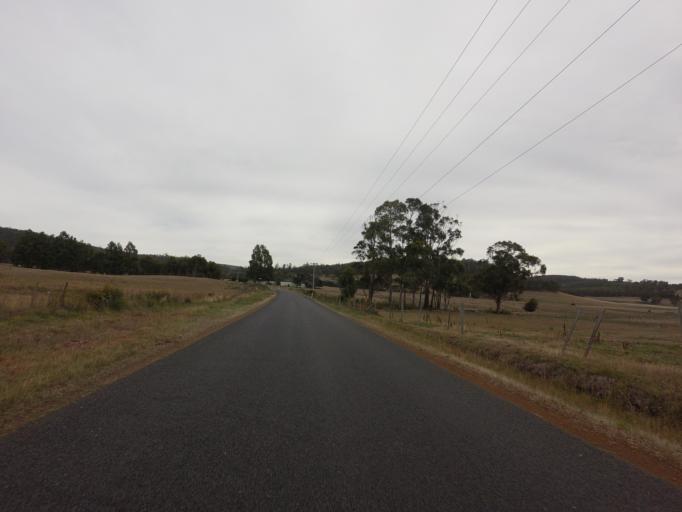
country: AU
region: Tasmania
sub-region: Sorell
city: Sorell
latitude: -42.5640
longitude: 147.5718
